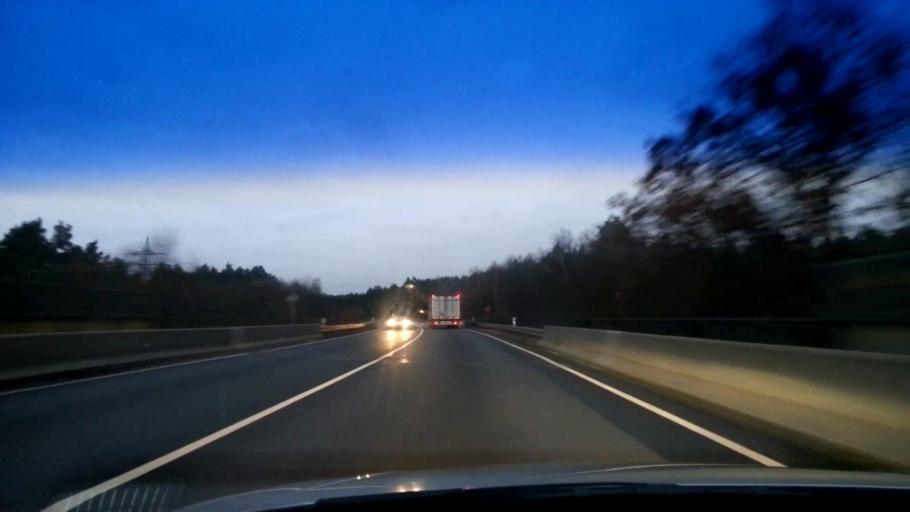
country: DE
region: Bavaria
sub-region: Upper Franconia
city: Strullendorf
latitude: 49.8506
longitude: 10.9556
